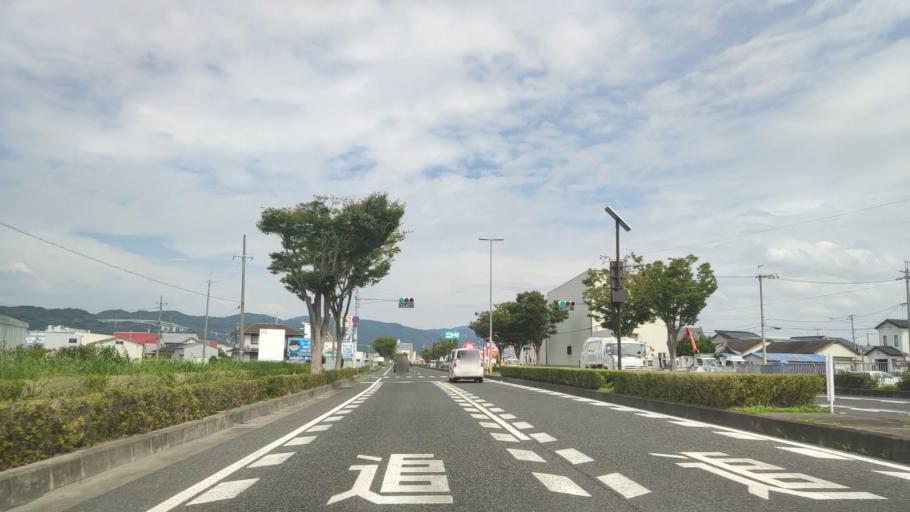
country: JP
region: Wakayama
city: Iwade
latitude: 34.2586
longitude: 135.2627
